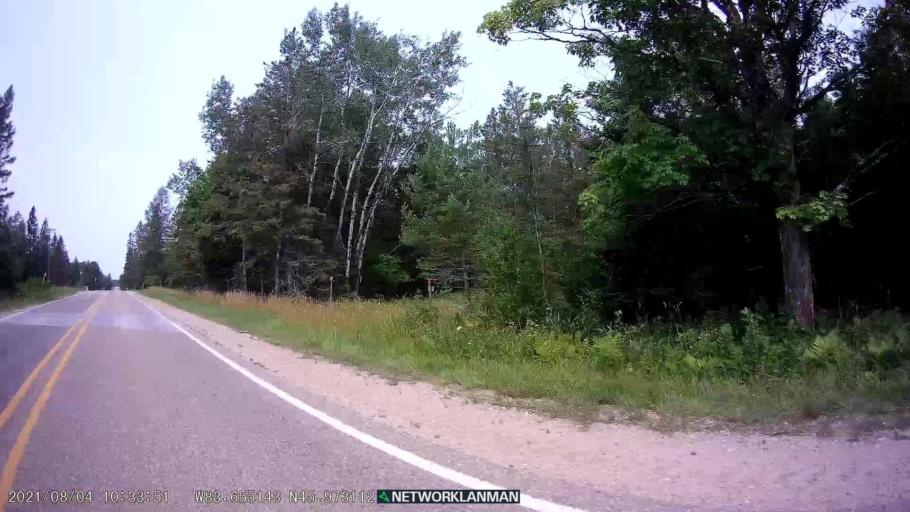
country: CA
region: Ontario
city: Thessalon
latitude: 45.9731
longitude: -83.6555
